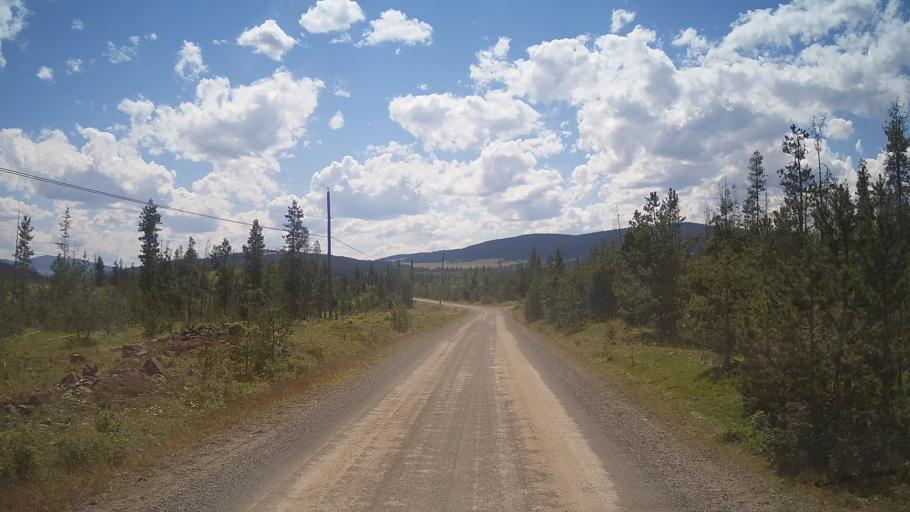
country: CA
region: British Columbia
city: Lillooet
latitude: 51.3340
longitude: -121.9733
